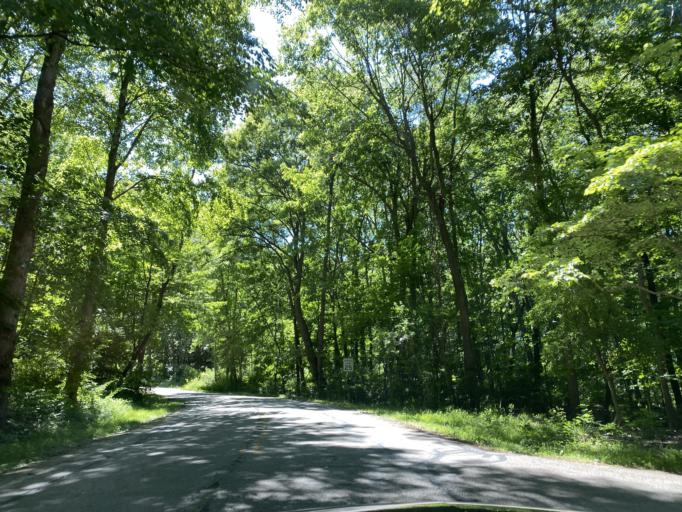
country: US
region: Ohio
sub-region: Summit County
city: Akron
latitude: 41.1281
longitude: -81.5426
